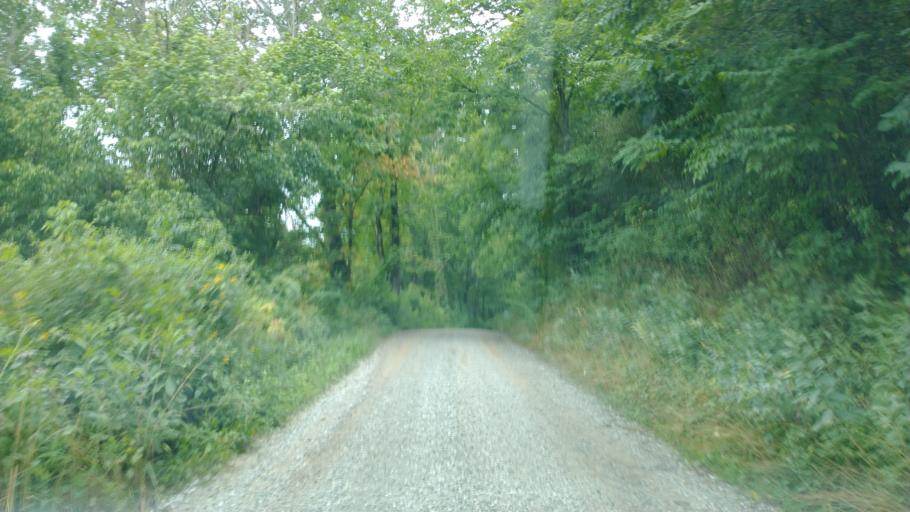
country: US
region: Ohio
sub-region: Meigs County
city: Middleport
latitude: 38.9225
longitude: -82.0514
